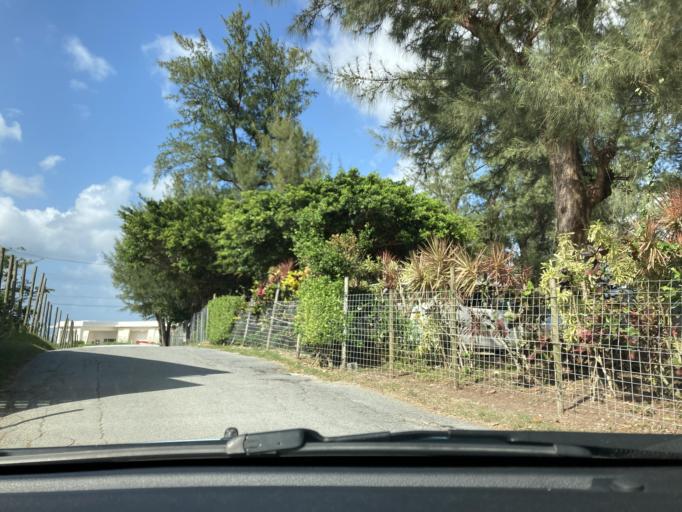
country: JP
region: Okinawa
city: Tomigusuku
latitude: 26.1857
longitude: 127.6828
